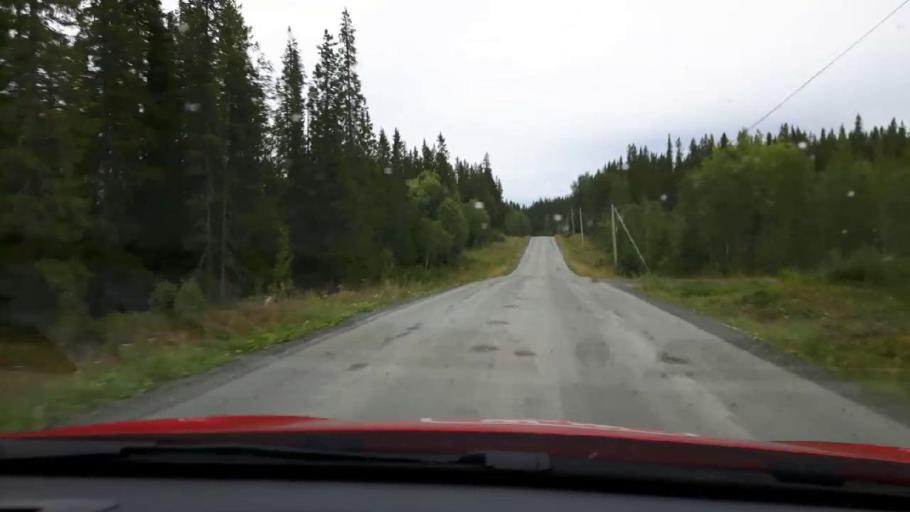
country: SE
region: Jaemtland
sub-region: Are Kommun
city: Jarpen
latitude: 63.4304
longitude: 13.3111
